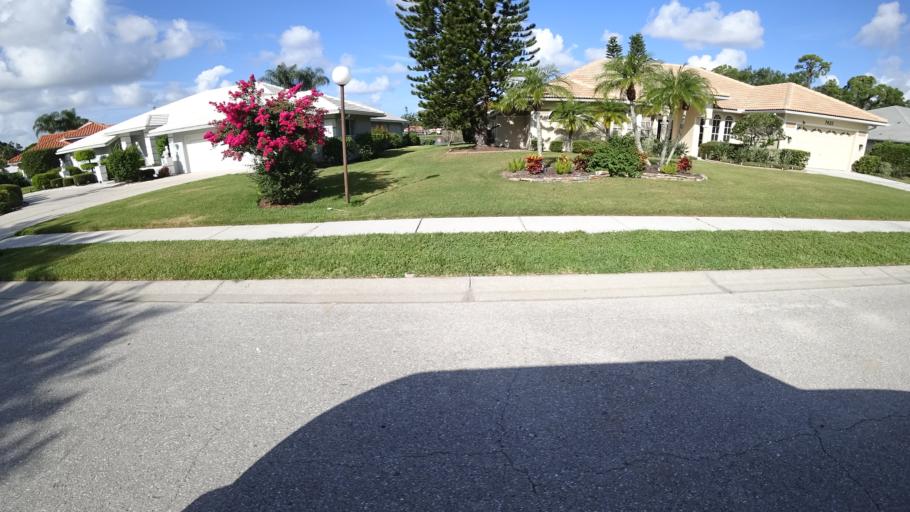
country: US
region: Florida
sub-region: Sarasota County
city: Desoto Lakes
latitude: 27.4074
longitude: -82.4823
